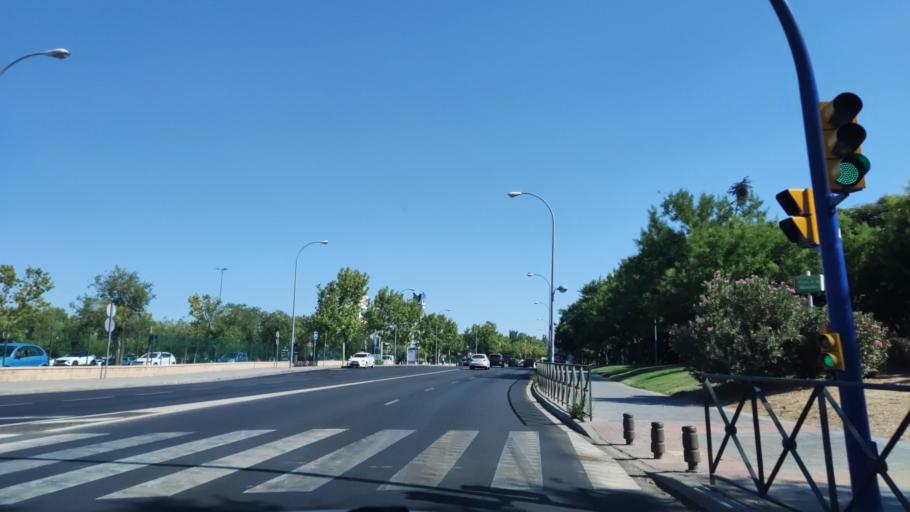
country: ES
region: Madrid
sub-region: Provincia de Madrid
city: Leganes
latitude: 40.3400
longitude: -3.7382
